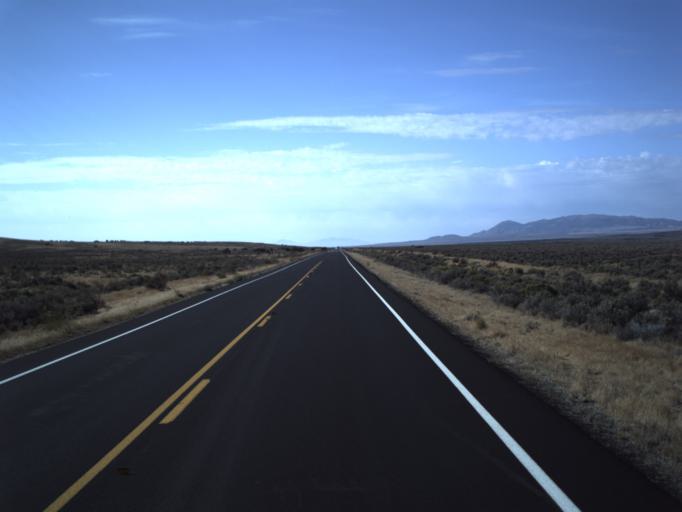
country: US
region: Idaho
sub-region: Cassia County
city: Burley
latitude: 41.7017
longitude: -113.5333
